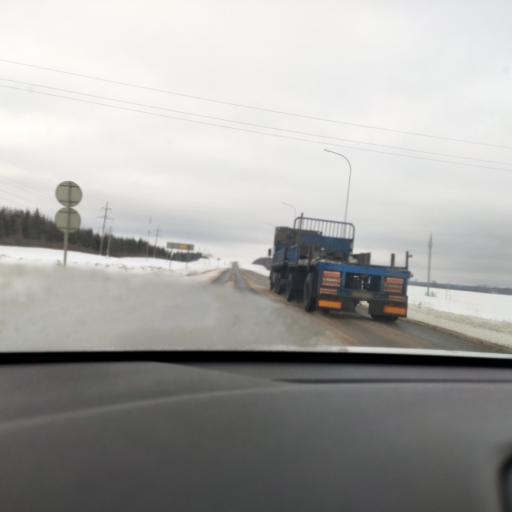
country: RU
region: Tatarstan
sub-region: Arskiy Rayon
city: Arsk
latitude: 56.2002
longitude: 49.9607
